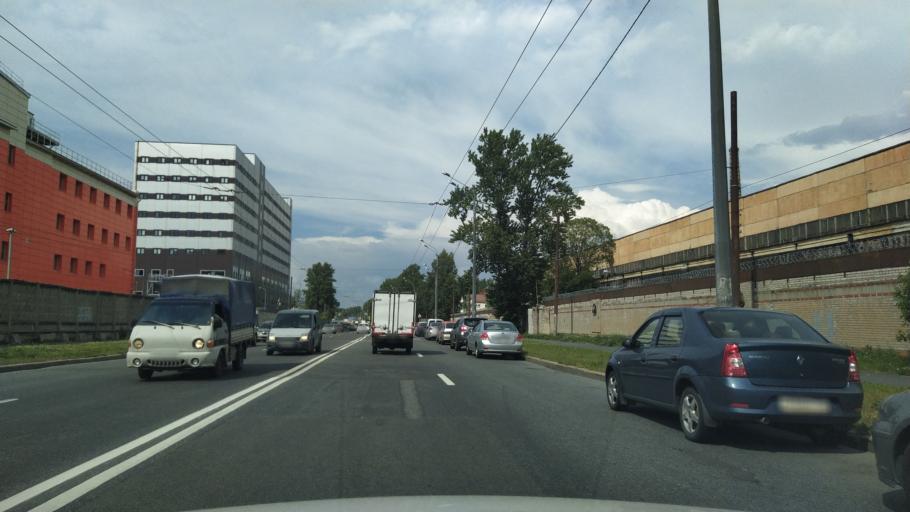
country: RU
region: Leningrad
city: Finlyandskiy
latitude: 59.9618
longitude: 30.3688
